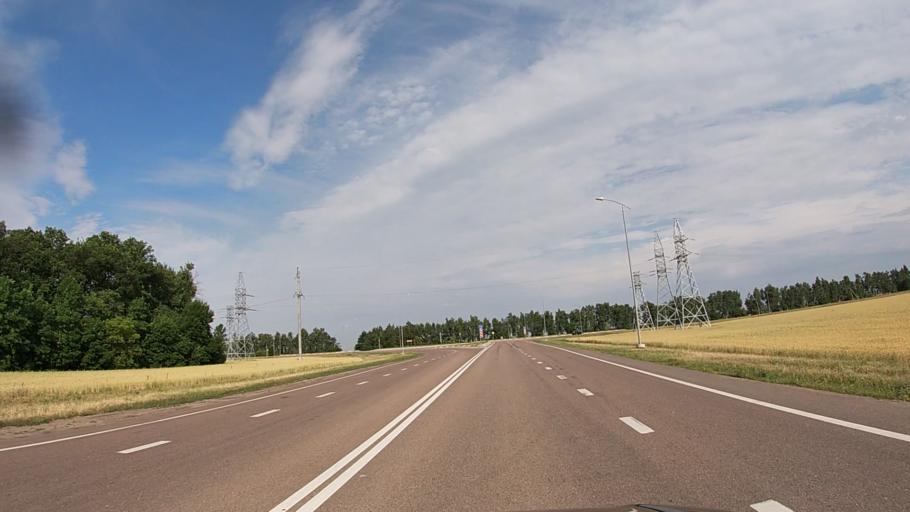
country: RU
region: Belgorod
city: Proletarskiy
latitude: 50.8303
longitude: 35.7691
